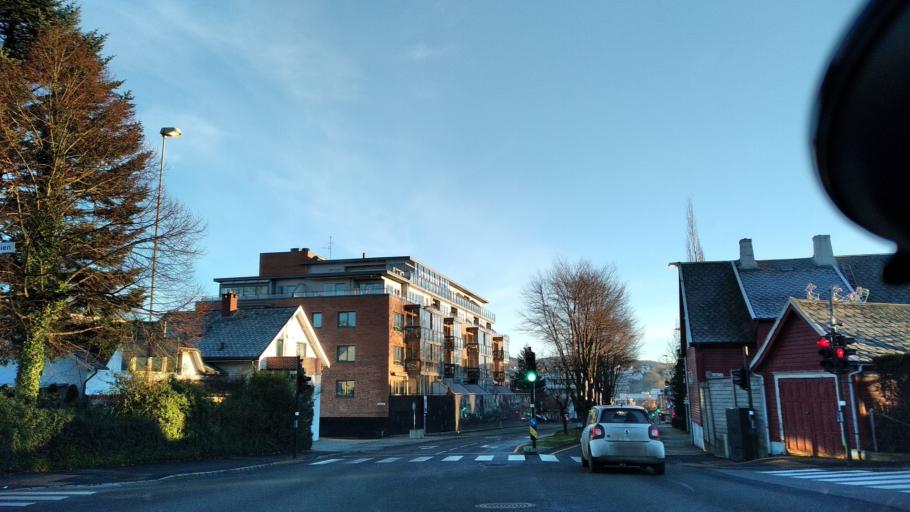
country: NO
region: Rogaland
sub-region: Sandnes
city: Sandnes
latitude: 58.8518
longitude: 5.7279
